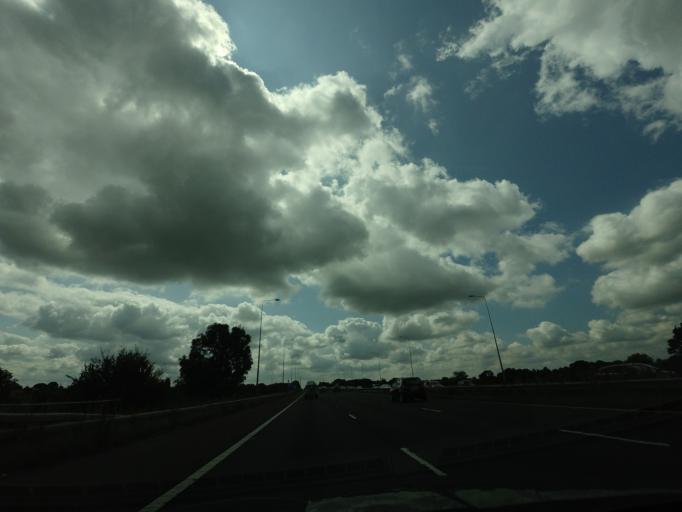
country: GB
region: England
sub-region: Borough of Wigan
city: Shevington
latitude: 53.6024
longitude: -2.6908
